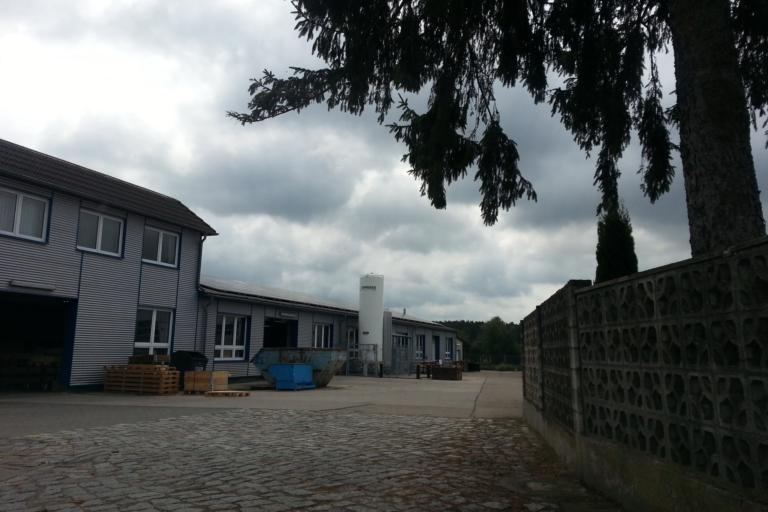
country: DE
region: Mecklenburg-Vorpommern
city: Torgelow
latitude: 53.6266
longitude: 13.9974
